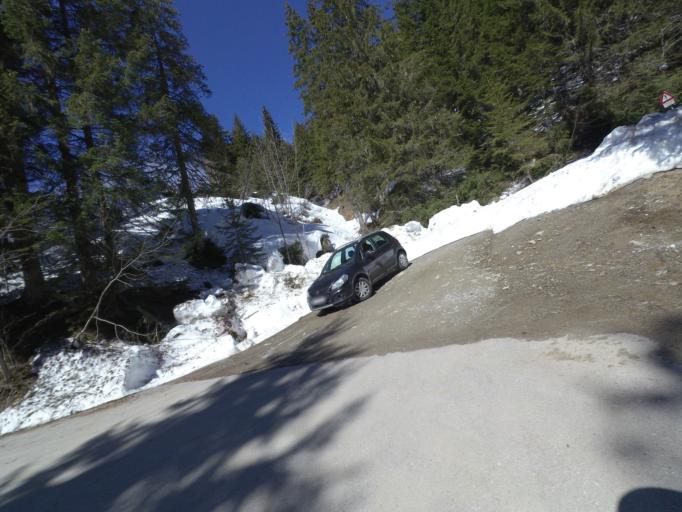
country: AT
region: Salzburg
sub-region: Politischer Bezirk Sankt Johann im Pongau
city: Sankt Veit im Pongau
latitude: 47.3434
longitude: 13.1609
